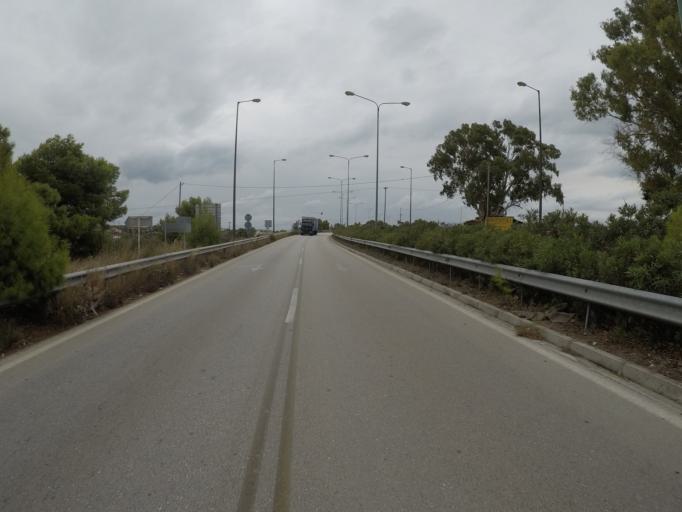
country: GR
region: Peloponnese
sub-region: Nomos Korinthias
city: Kyras Vrysi
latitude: 37.9315
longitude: 22.9928
